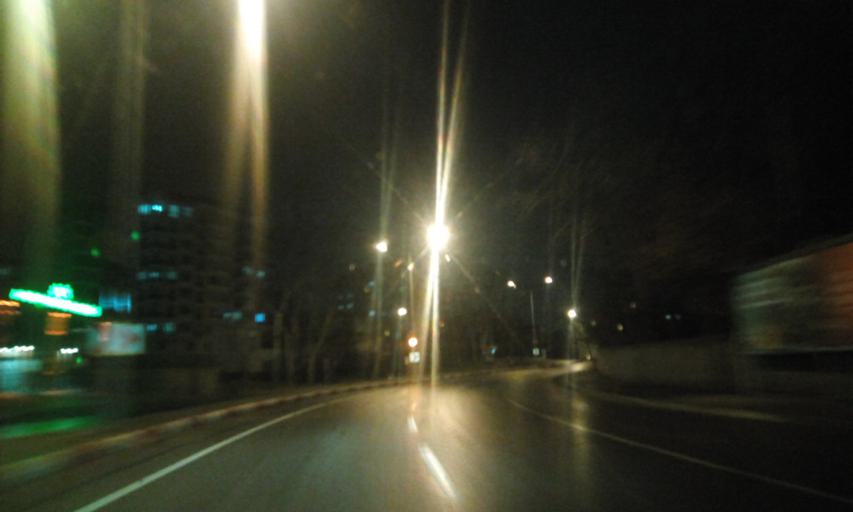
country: TR
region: Istanbul
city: Sultanbeyli
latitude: 40.9350
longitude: 29.2730
